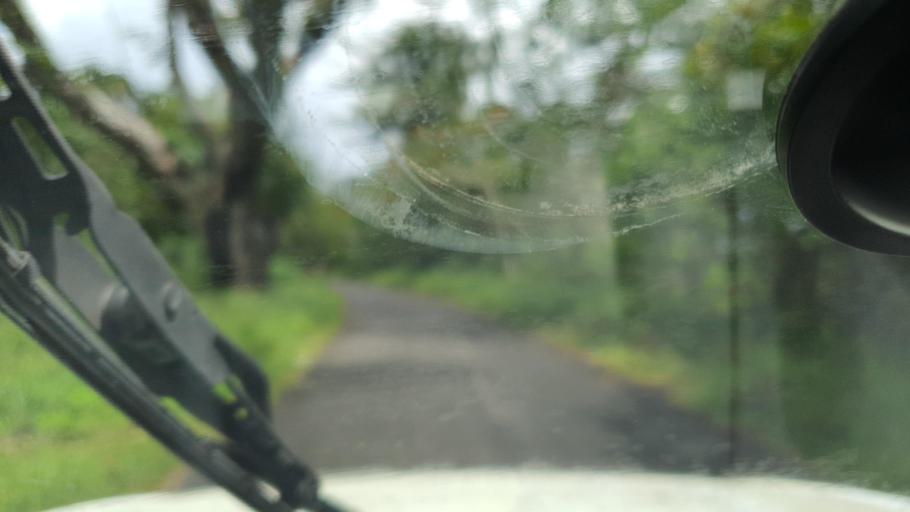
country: SB
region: Guadalcanal
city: Honiara
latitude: -9.2735
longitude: 159.7343
